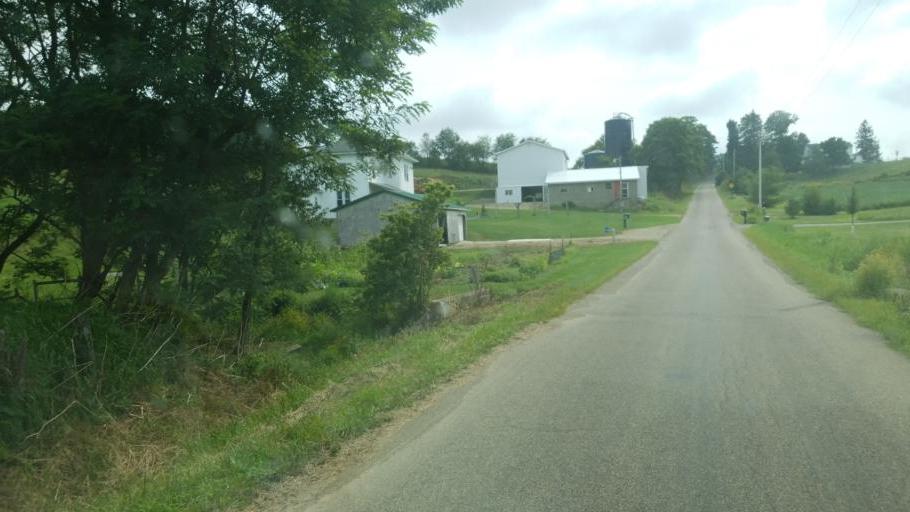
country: US
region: Ohio
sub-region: Knox County
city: Danville
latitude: 40.4964
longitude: -82.3413
